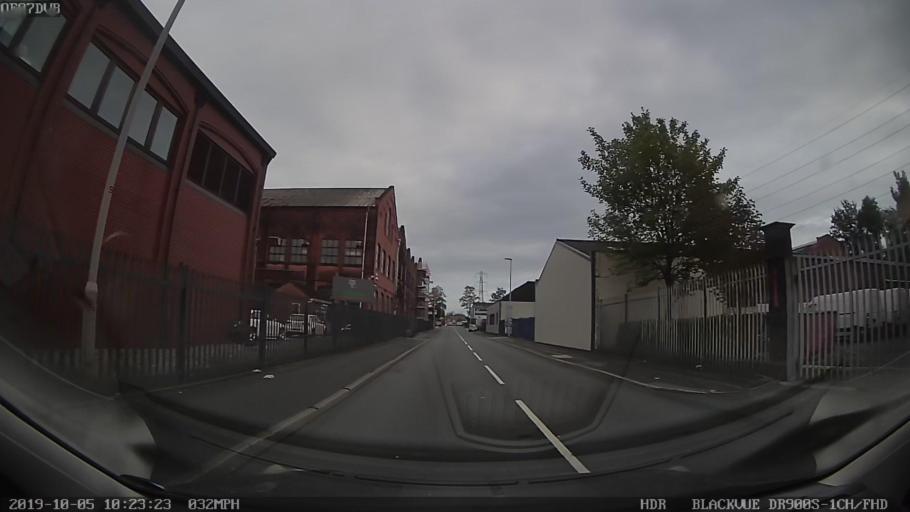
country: GB
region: England
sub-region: Borough of Rochdale
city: Middleton
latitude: 53.5490
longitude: -2.1697
